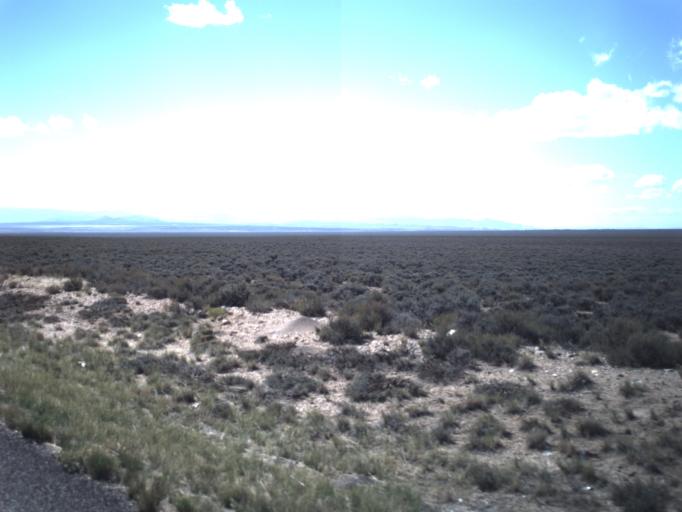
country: US
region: Utah
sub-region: Iron County
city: Enoch
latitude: 37.9780
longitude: -113.0042
